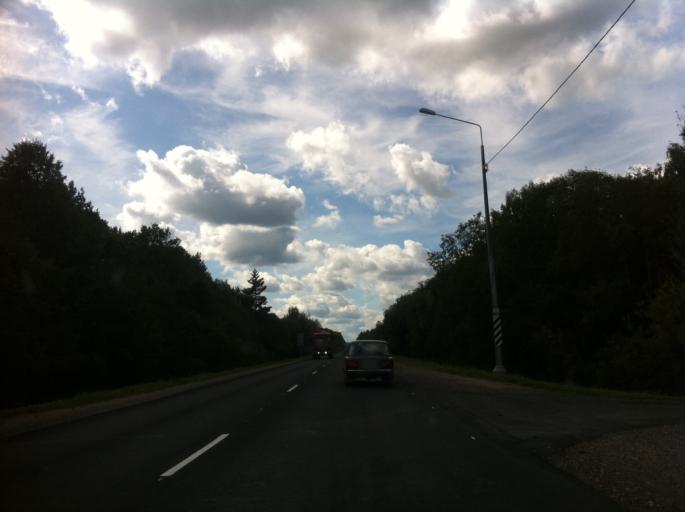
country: RU
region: Pskov
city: Izborsk
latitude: 57.7152
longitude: 27.9137
